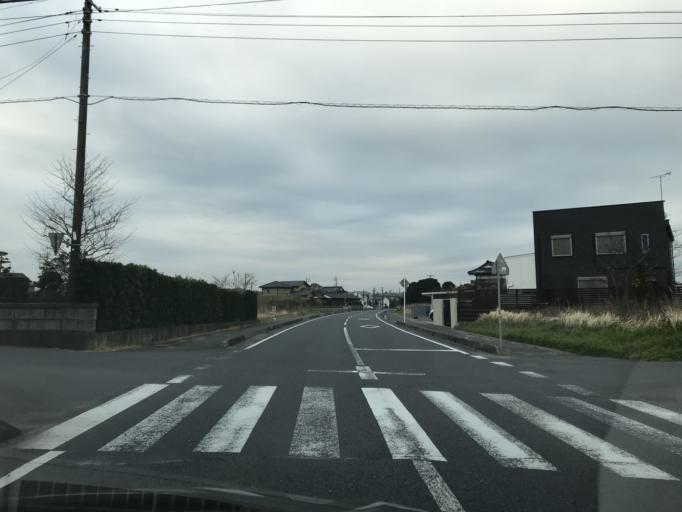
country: JP
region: Ibaraki
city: Kashima-shi
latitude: 35.9147
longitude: 140.6283
